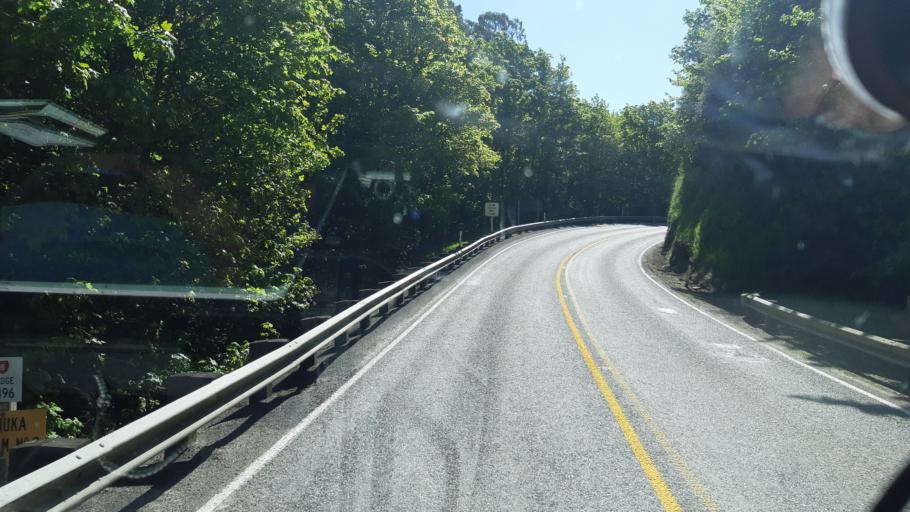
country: NZ
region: Otago
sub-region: Clutha District
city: Milton
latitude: -46.0723
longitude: 169.8374
